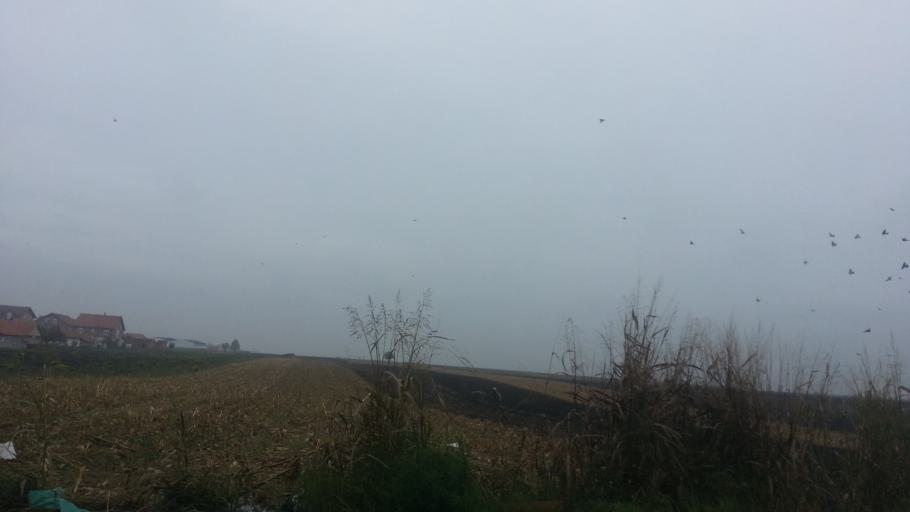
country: RS
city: Novi Banovci
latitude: 44.9060
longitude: 20.2976
